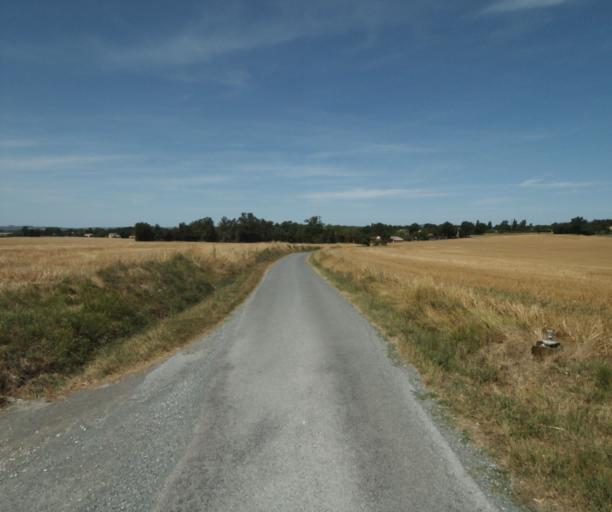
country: FR
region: Midi-Pyrenees
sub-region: Departement du Tarn
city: Soreze
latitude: 43.4857
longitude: 2.0573
